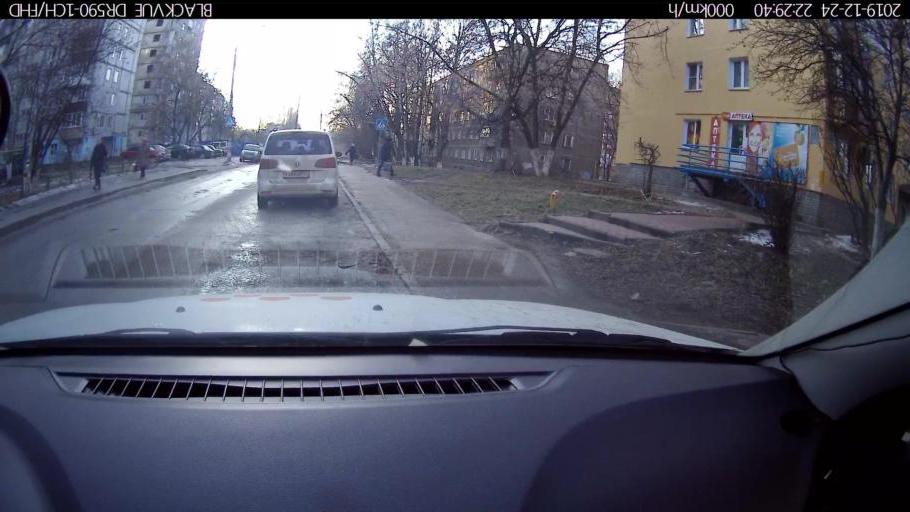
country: RU
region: Nizjnij Novgorod
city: Nizhniy Novgorod
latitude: 56.2364
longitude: 43.9606
